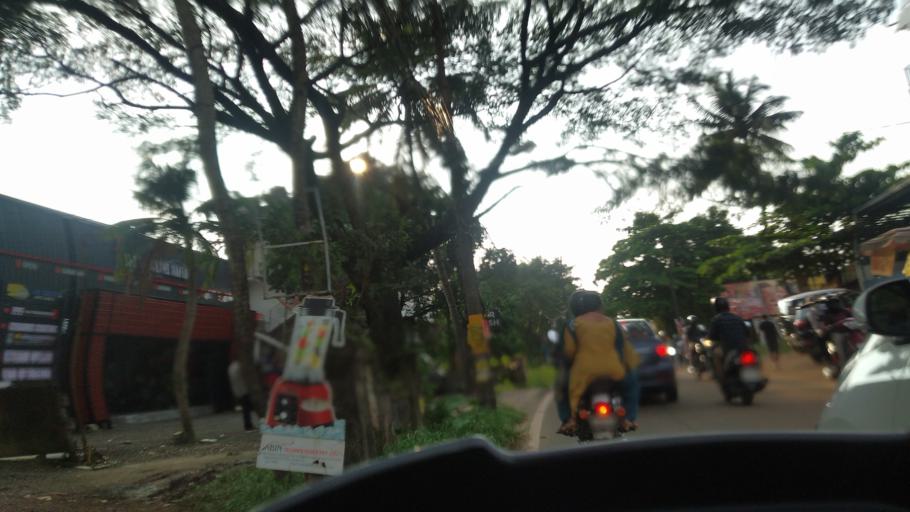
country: IN
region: Kerala
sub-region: Ernakulam
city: Cochin
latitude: 9.9832
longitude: 76.2999
